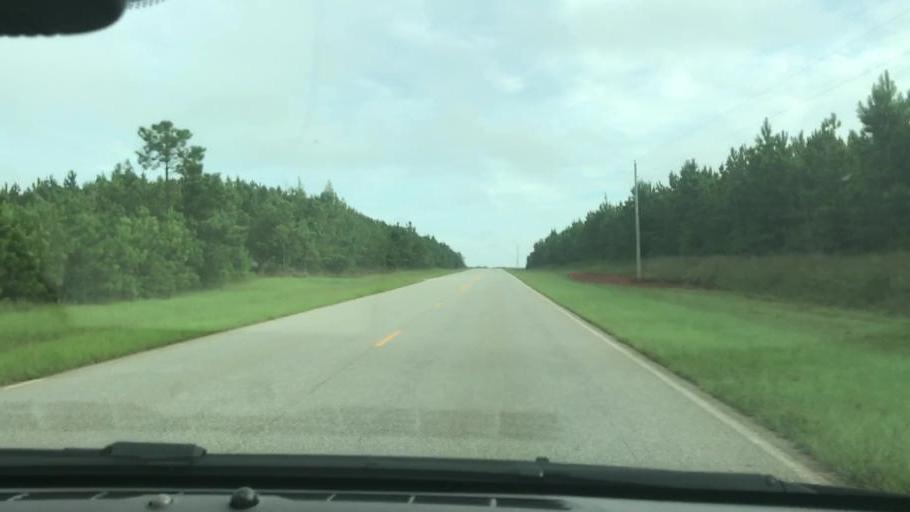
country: US
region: Georgia
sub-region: Stewart County
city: Lumpkin
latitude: 32.0077
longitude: -84.9318
